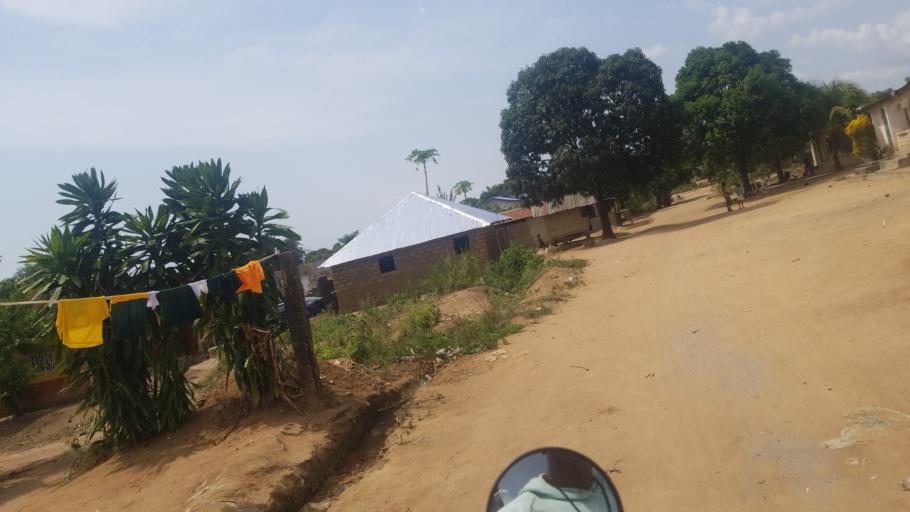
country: SL
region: Western Area
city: Waterloo
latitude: 8.3148
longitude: -13.0486
